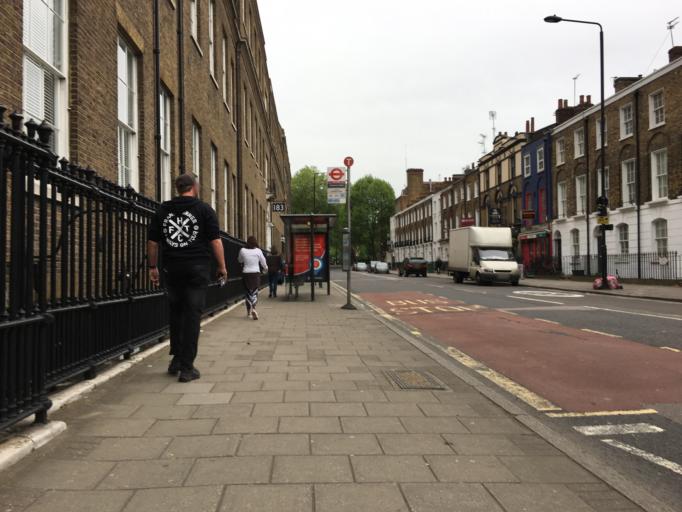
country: GB
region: England
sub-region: Greater London
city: Camden Town
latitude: 51.5318
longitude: -0.1351
